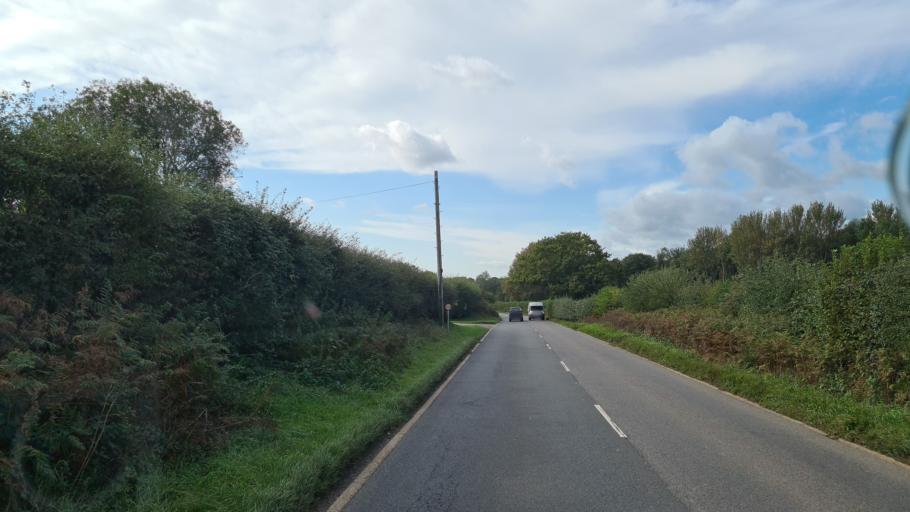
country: GB
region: England
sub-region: East Sussex
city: Bodle Street
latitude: 50.8851
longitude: 0.3034
